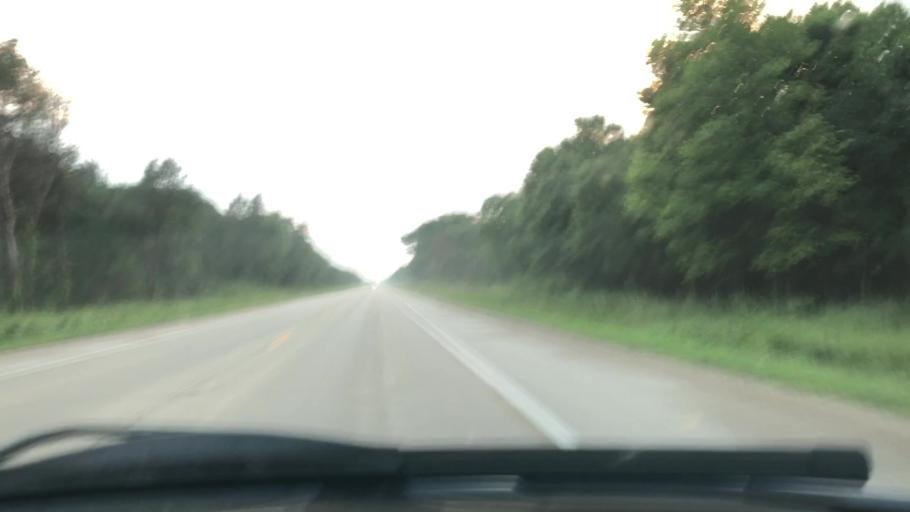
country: US
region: Wisconsin
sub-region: Sauk County
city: Spring Green
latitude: 43.1912
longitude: -90.1772
